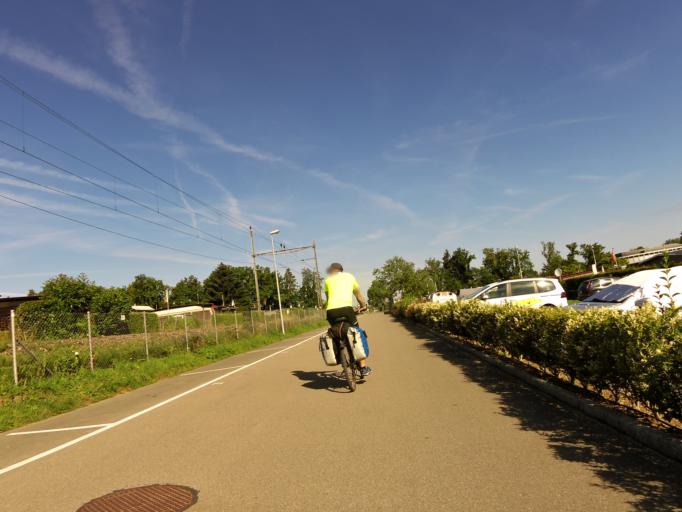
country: CH
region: Thurgau
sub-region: Arbon District
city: Uttwil
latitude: 47.5889
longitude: 9.3330
